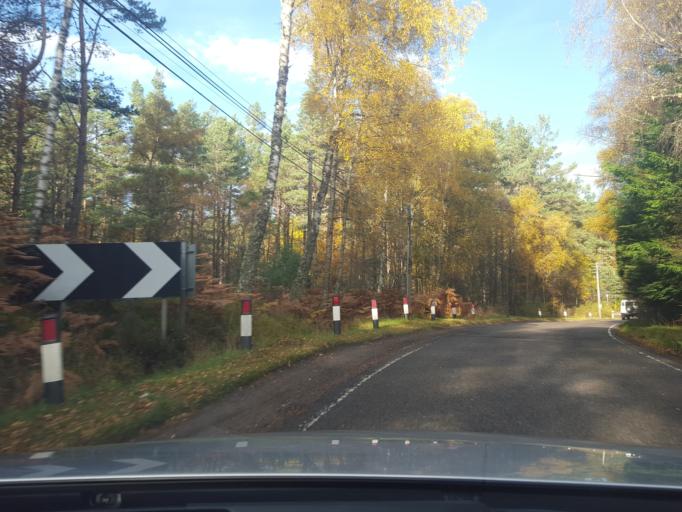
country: GB
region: Scotland
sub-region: Highland
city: Spean Bridge
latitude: 57.1770
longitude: -4.8004
